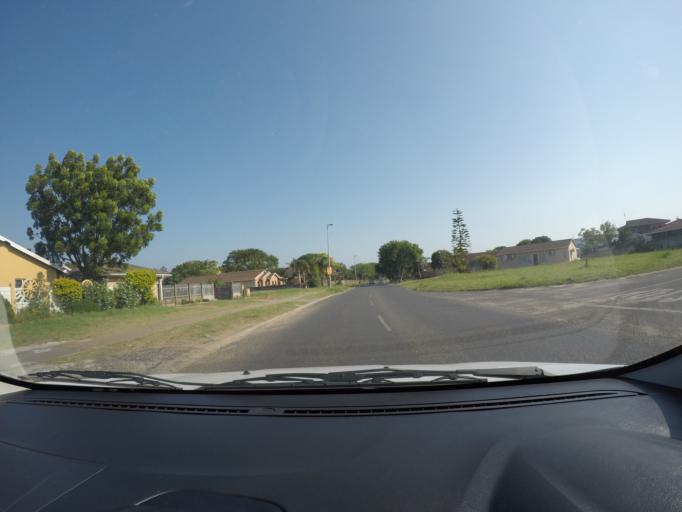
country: ZA
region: KwaZulu-Natal
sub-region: uThungulu District Municipality
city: Richards Bay
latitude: -28.7252
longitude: 32.0418
